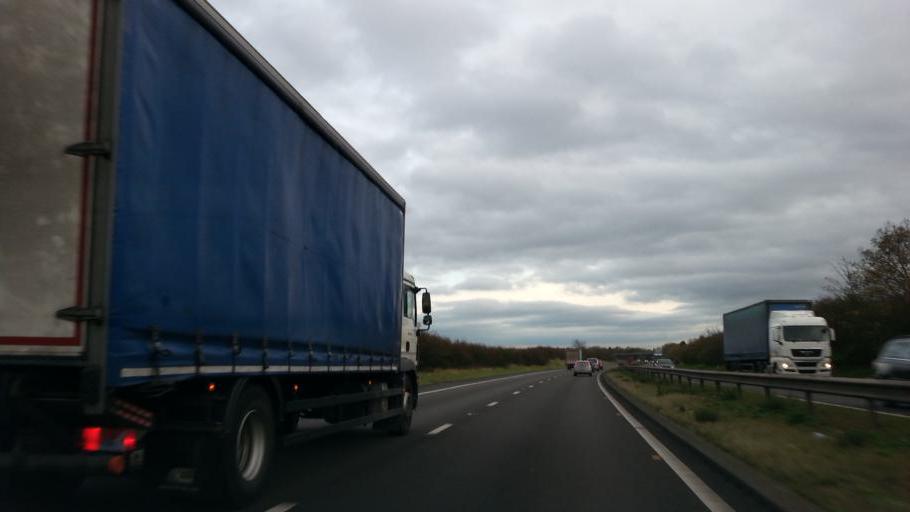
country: GB
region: England
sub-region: Doncaster
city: Tickhill
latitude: 53.4428
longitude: -1.1037
